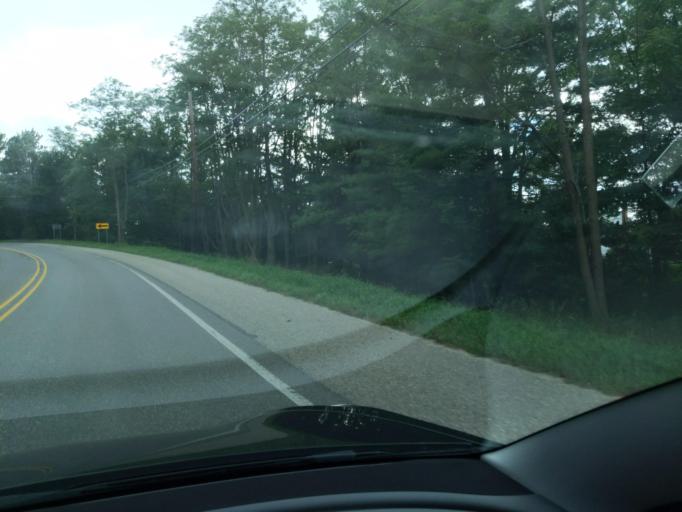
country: US
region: Michigan
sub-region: Kalkaska County
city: Rapid City
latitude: 44.8755
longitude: -85.2787
